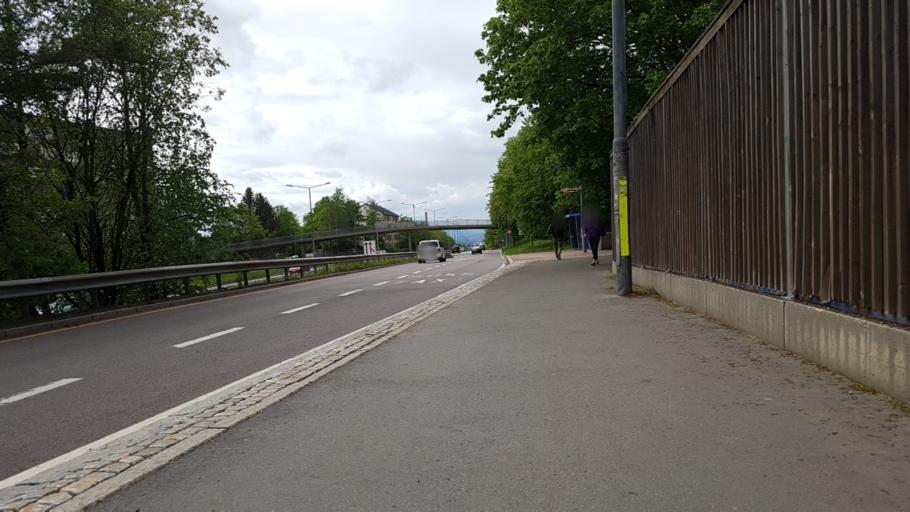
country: NO
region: Oslo
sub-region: Oslo
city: Oslo
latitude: 59.9428
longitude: 10.8086
